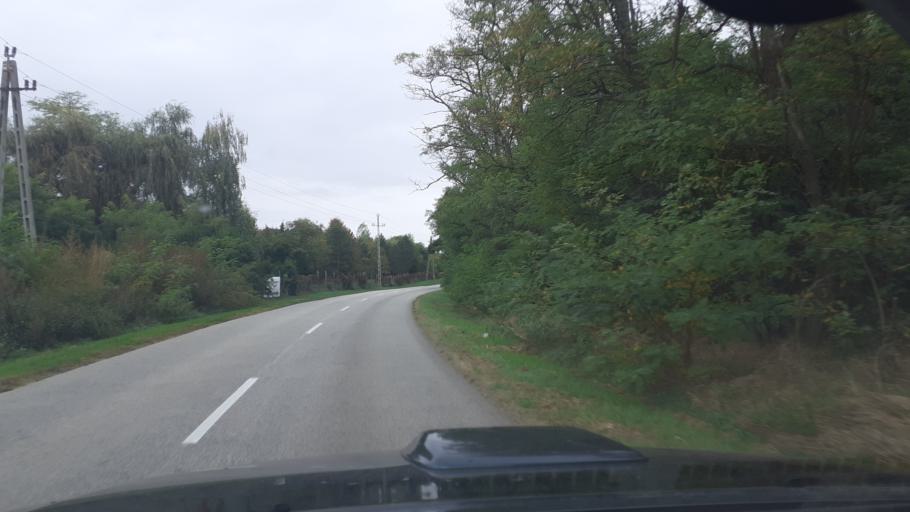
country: HU
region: Tolna
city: Dunafoldvar
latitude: 46.8325
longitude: 18.9030
